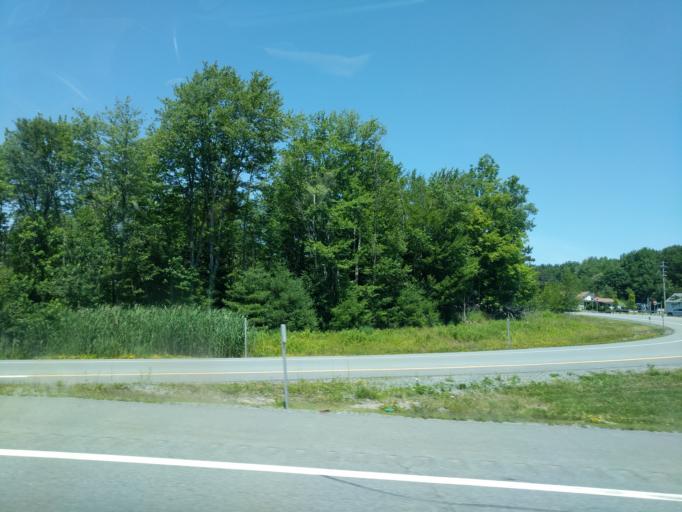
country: US
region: New York
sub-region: Sullivan County
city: Monticello
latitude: 41.6432
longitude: -74.6464
